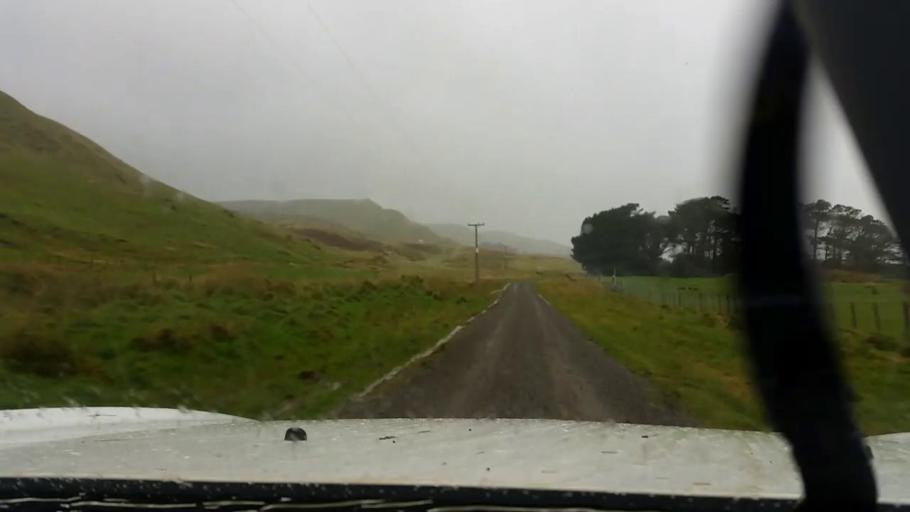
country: NZ
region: Wellington
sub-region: Masterton District
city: Masterton
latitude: -41.2542
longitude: 175.9103
